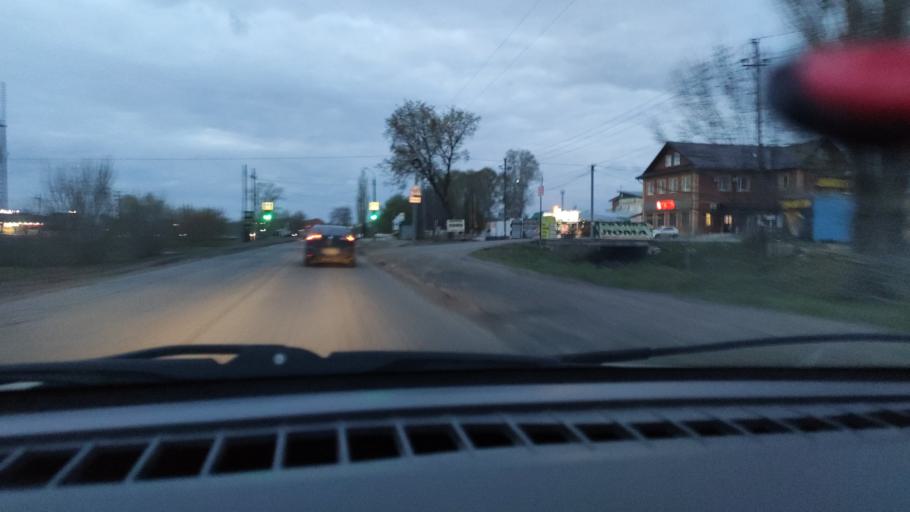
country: RU
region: Orenburg
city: Tatarskaya Kargala
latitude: 51.8657
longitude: 55.1399
